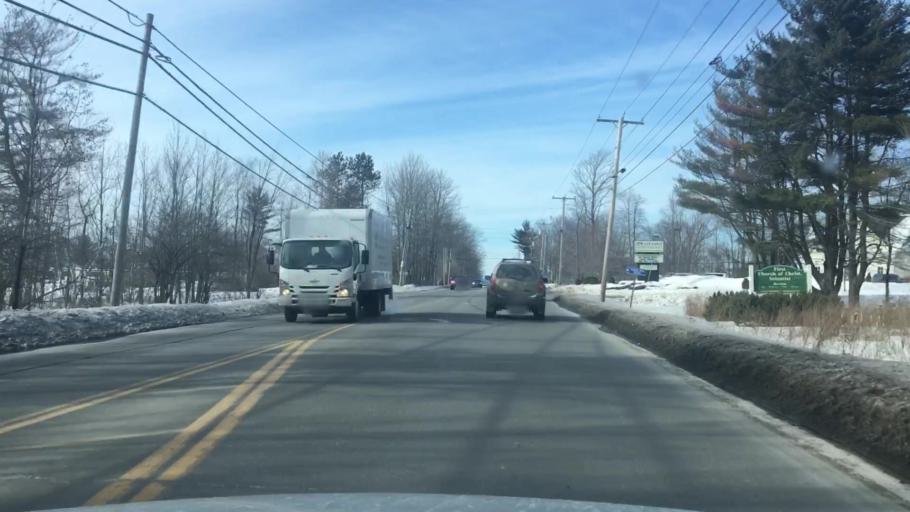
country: US
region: Maine
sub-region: Penobscot County
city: Bangor
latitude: 44.8307
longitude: -68.7861
